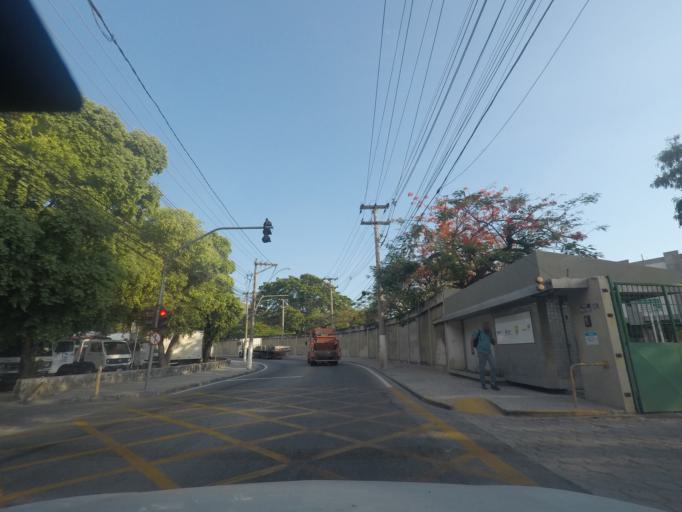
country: BR
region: Rio de Janeiro
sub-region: Niteroi
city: Niteroi
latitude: -22.8778
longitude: -43.1139
